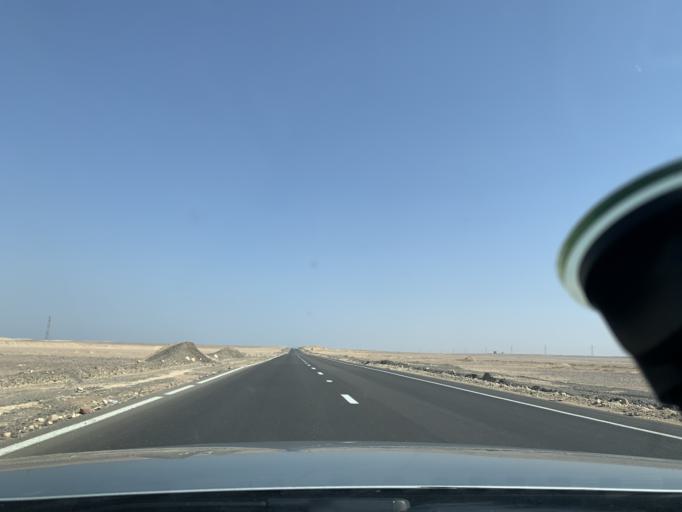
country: EG
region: As Suways
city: Ain Sukhna
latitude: 28.7940
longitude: 32.7465
